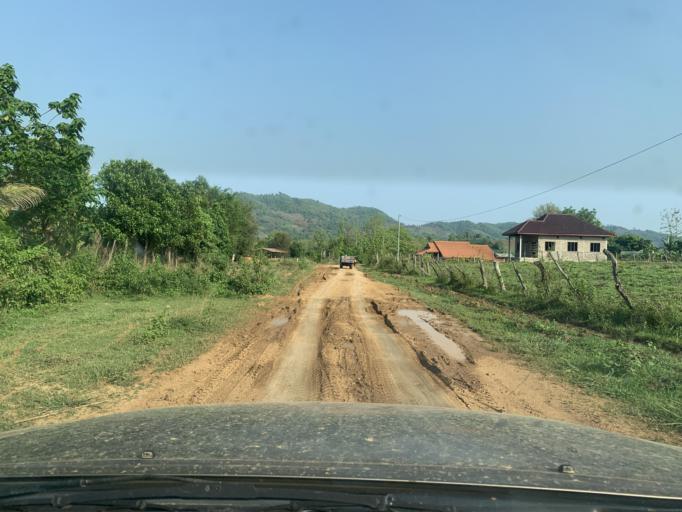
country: TH
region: Uttaradit
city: Ban Khok
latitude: 18.2715
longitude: 101.3079
